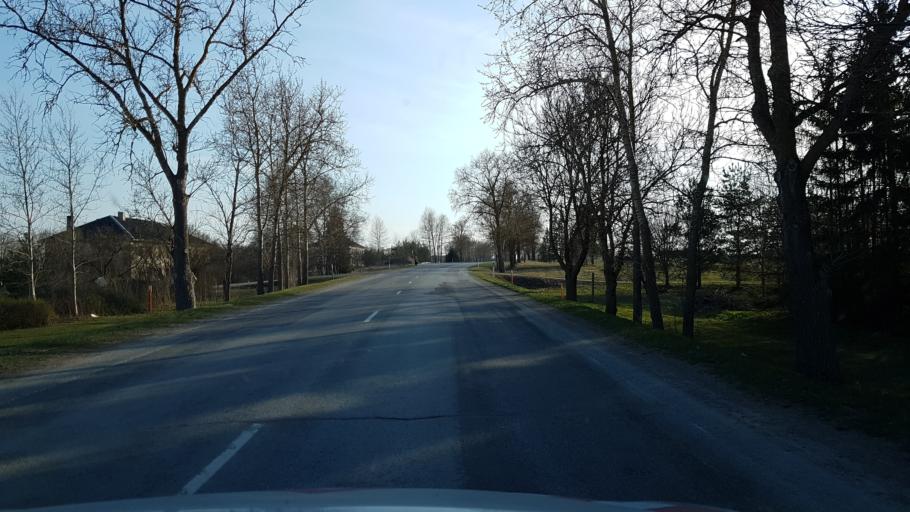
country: EE
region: Laeaene-Virumaa
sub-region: Rakvere linn
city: Rakvere
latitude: 59.3702
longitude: 26.3806
